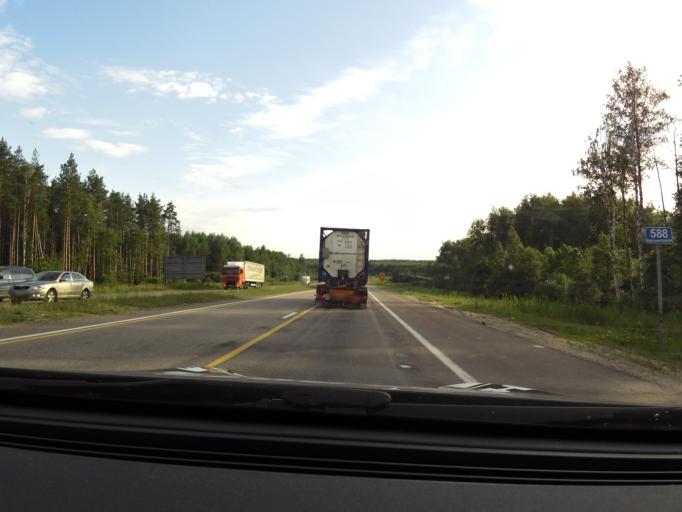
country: RU
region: Vladimir
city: Sudogda
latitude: 56.1295
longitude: 40.8750
